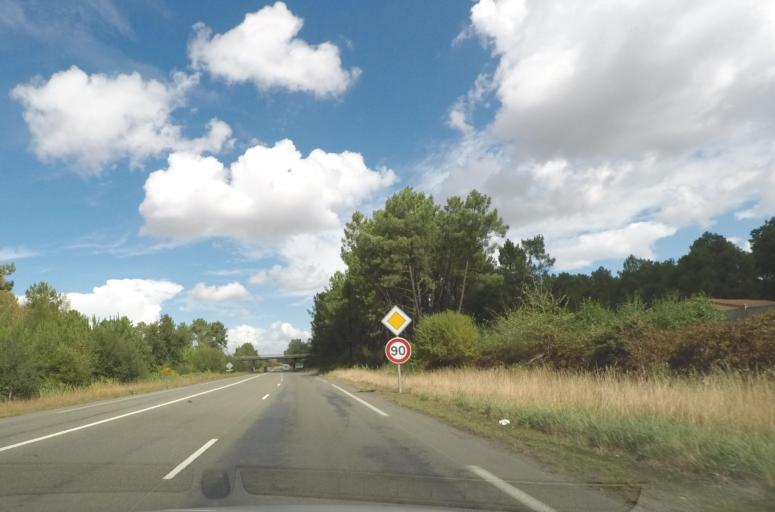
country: FR
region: Pays de la Loire
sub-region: Departement de la Sarthe
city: Spay
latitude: 47.9050
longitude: 0.1610
